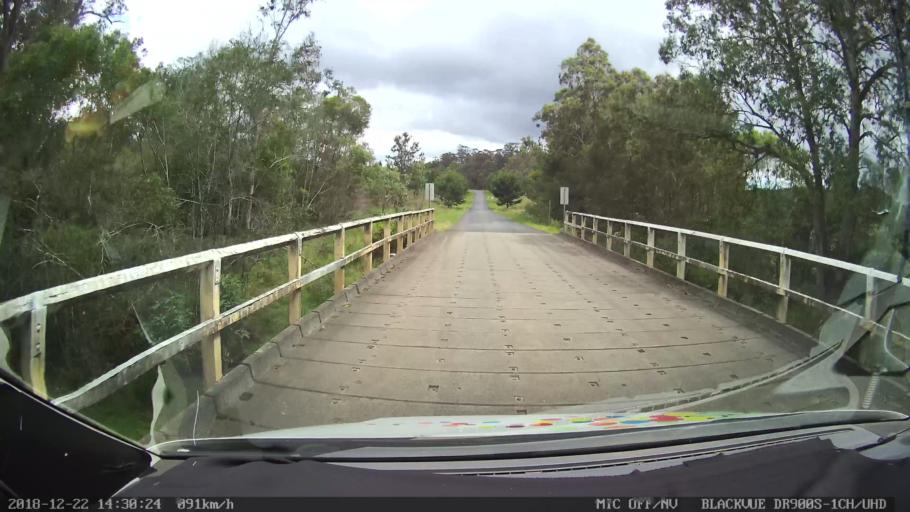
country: AU
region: New South Wales
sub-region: Bellingen
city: Dorrigo
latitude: -30.0859
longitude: 152.6316
